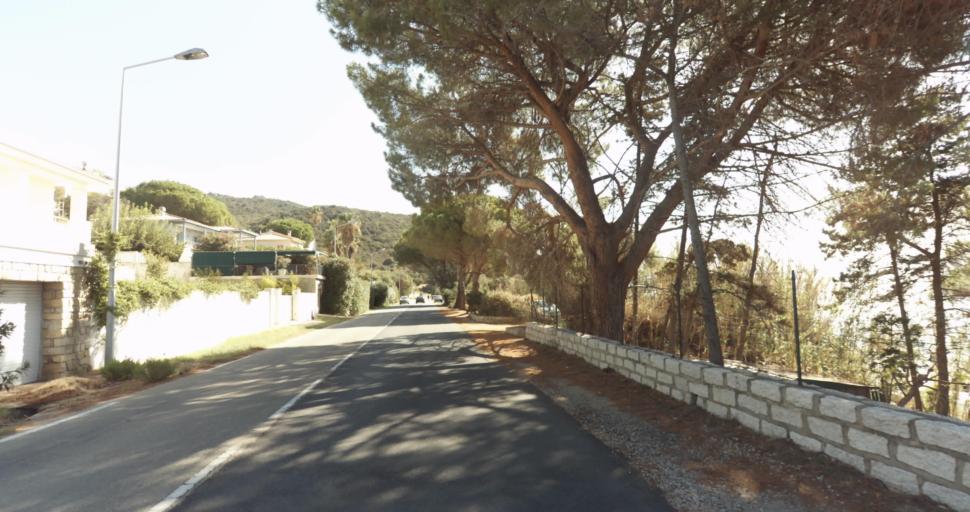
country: FR
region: Corsica
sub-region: Departement de la Corse-du-Sud
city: Ajaccio
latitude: 41.9094
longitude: 8.6521
